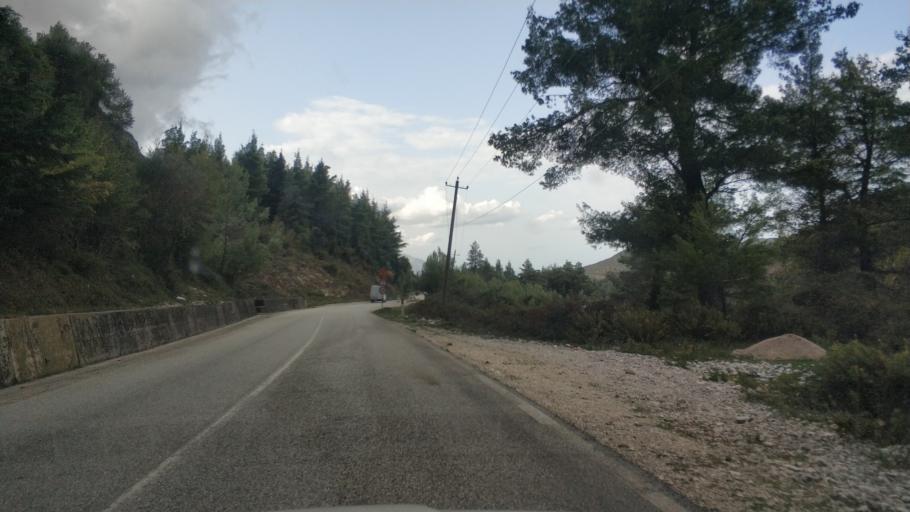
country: AL
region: Vlore
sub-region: Rrethi i Vlores
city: Orikum
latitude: 40.2573
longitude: 19.5282
